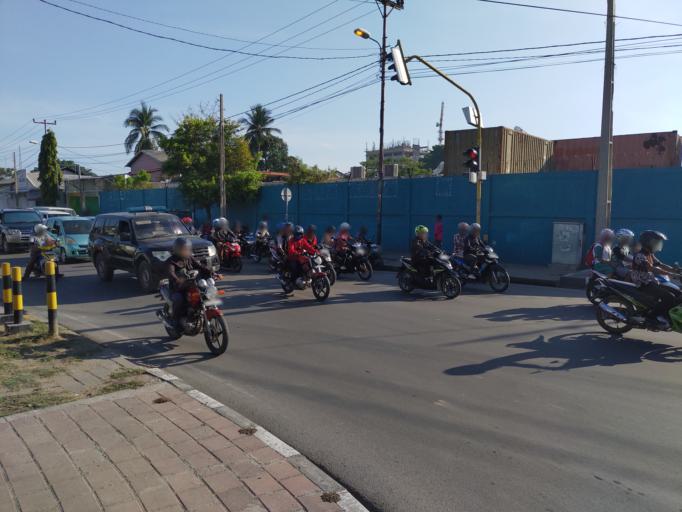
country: TL
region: Dili
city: Dili
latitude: -8.5575
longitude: 125.5719
